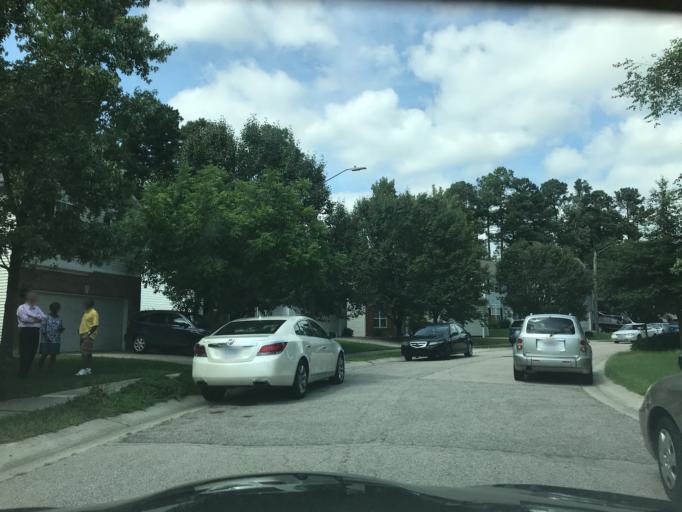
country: US
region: North Carolina
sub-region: Wake County
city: Rolesville
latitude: 35.8881
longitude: -78.5474
